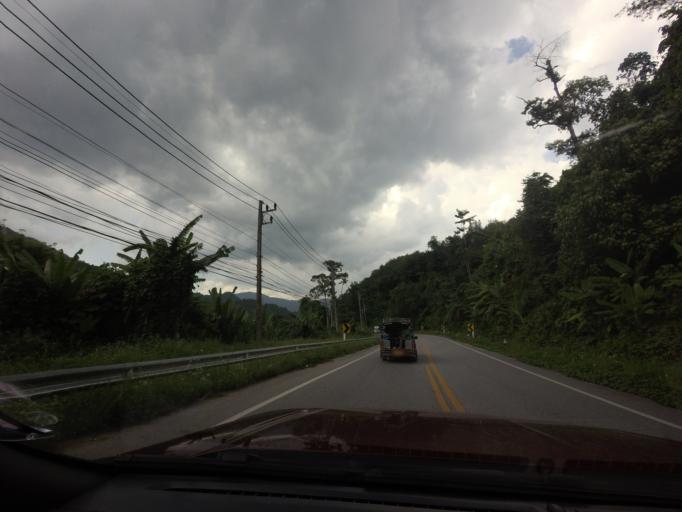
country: TH
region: Yala
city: Than To
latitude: 6.2247
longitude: 101.1653
